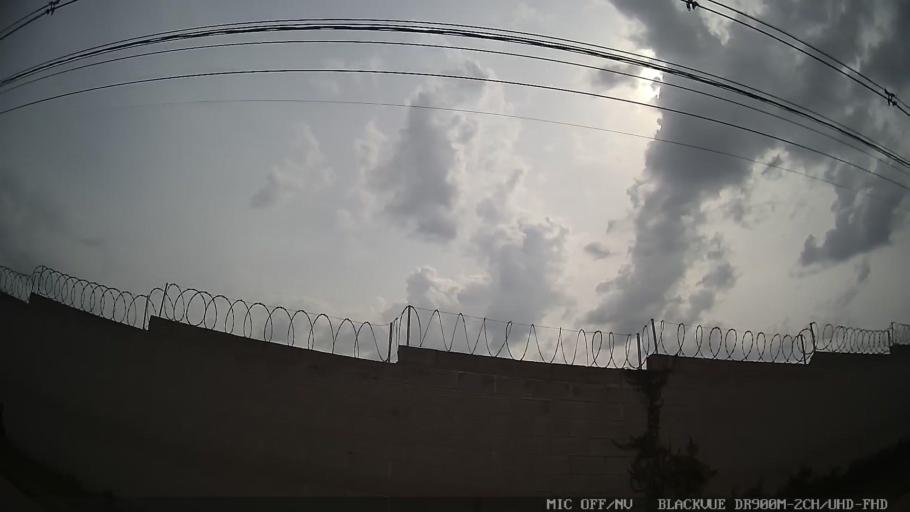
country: BR
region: Sao Paulo
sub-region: Indaiatuba
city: Indaiatuba
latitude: -23.1033
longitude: -47.2590
